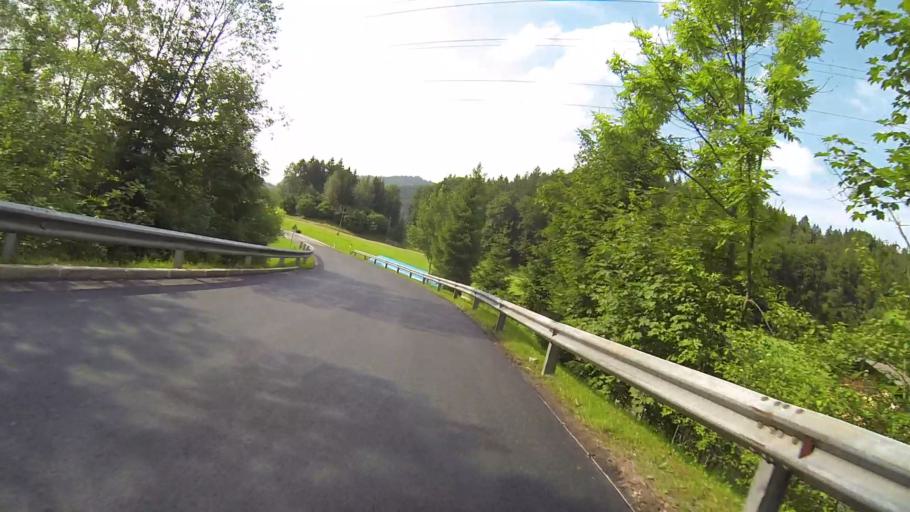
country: AT
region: Tyrol
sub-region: Politischer Bezirk Reutte
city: Pflach
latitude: 47.5281
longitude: 10.7033
